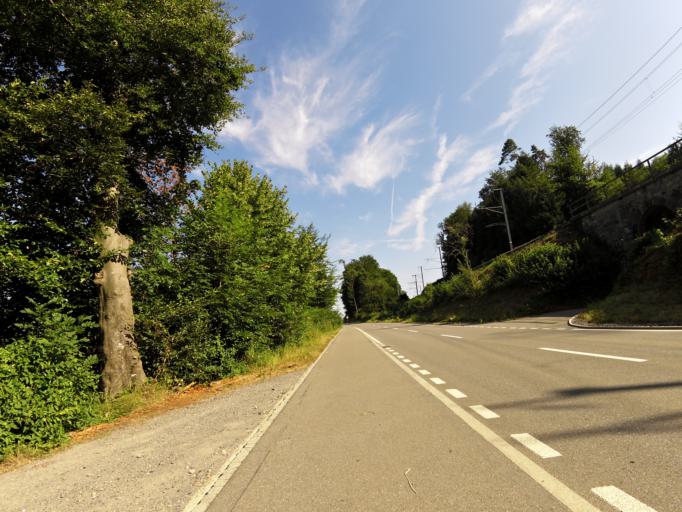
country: CH
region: Zug
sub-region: Zug
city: Walchwil
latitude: 47.1209
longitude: 8.4962
